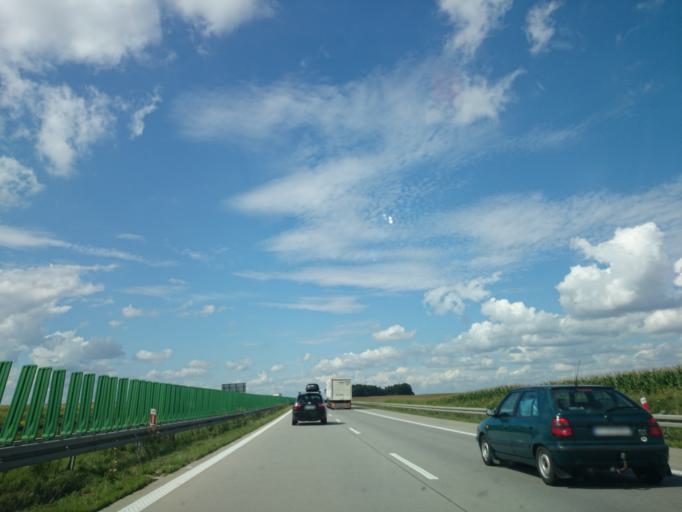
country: PL
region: Lower Silesian Voivodeship
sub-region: Powiat legnicki
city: Legnickie Pole
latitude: 51.1293
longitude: 16.3191
